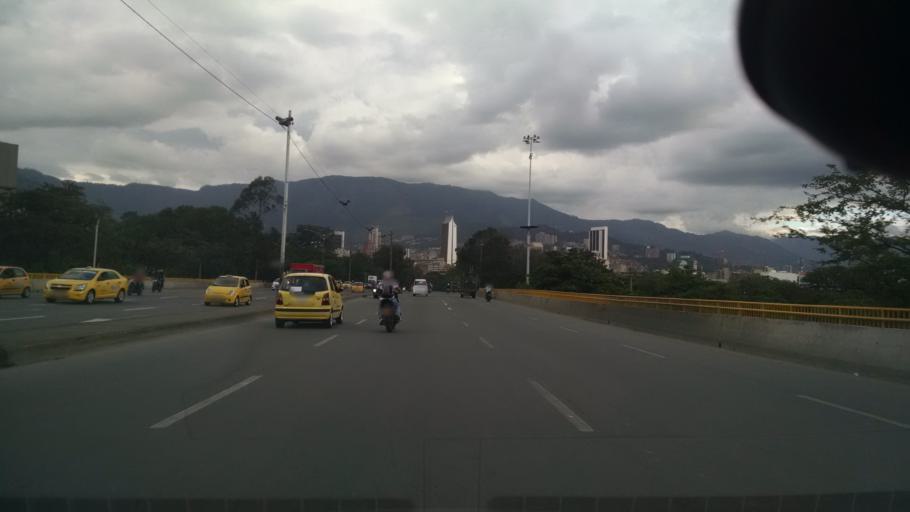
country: CO
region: Antioquia
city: Medellin
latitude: 6.2611
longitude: -75.5739
